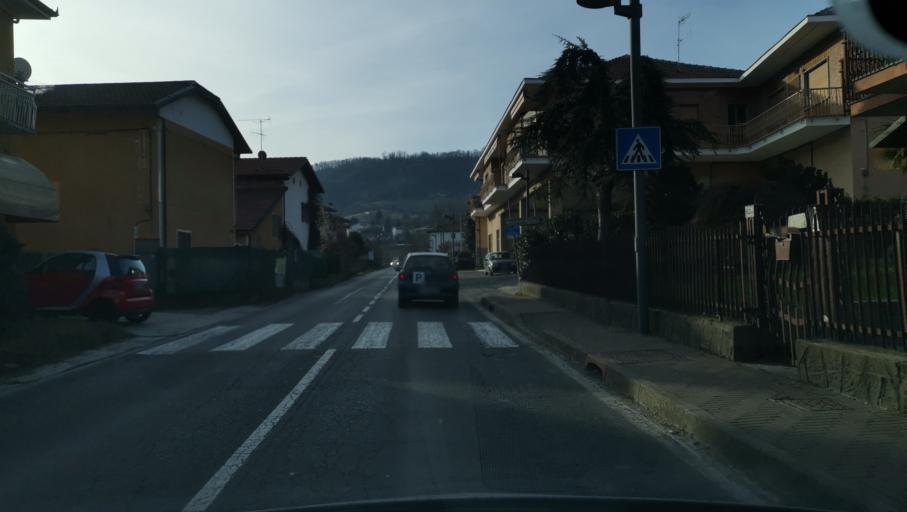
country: IT
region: Piedmont
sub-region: Provincia di Torino
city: Castiglione Torinese
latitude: 45.1093
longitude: 7.8164
